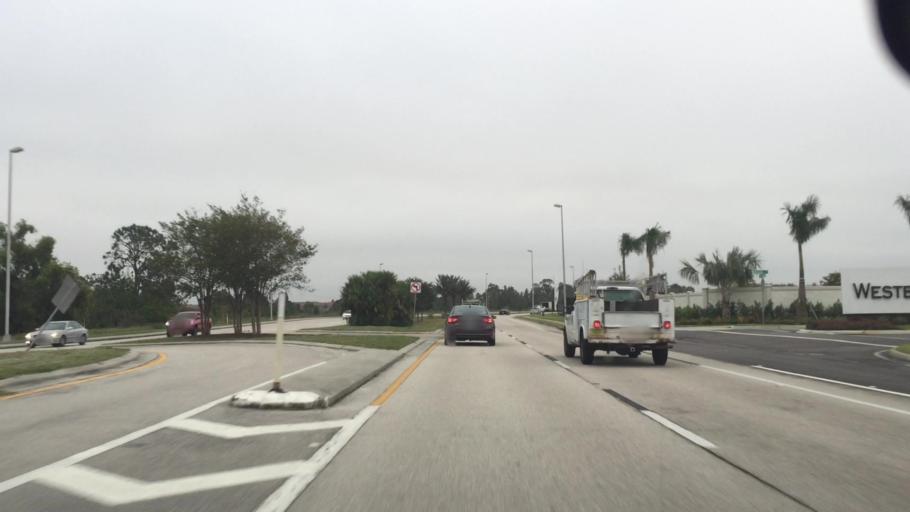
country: US
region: Florida
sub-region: Lee County
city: Three Oaks
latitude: 26.4896
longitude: -81.8002
